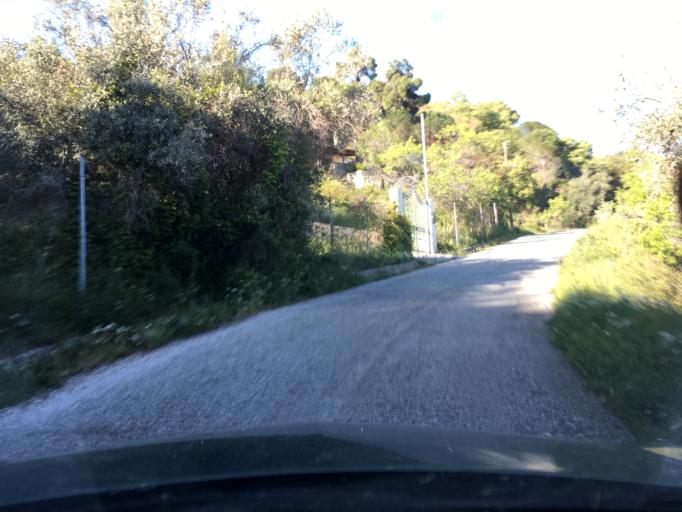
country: GR
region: Thessaly
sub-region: Nomos Magnisias
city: Skopelos
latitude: 39.1787
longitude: 23.6209
